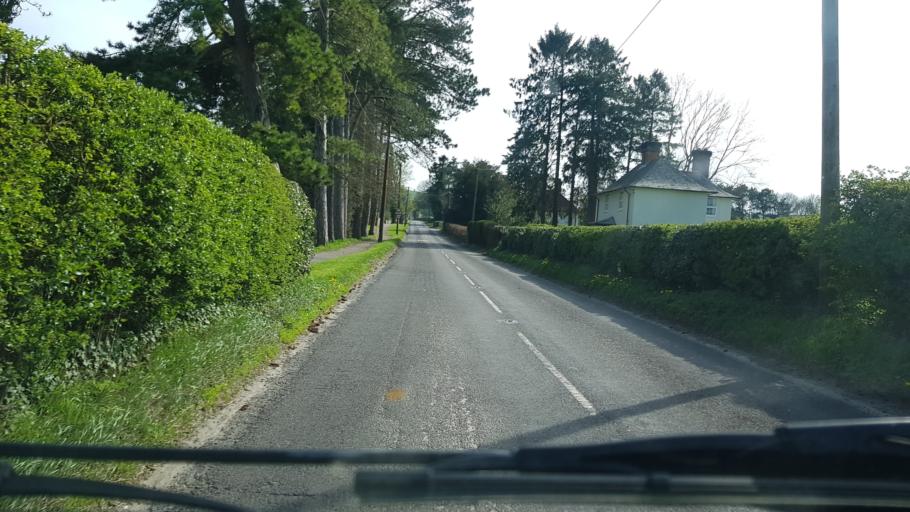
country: GB
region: England
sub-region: Hampshire
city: Kingsclere
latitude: 51.3188
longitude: -1.2521
